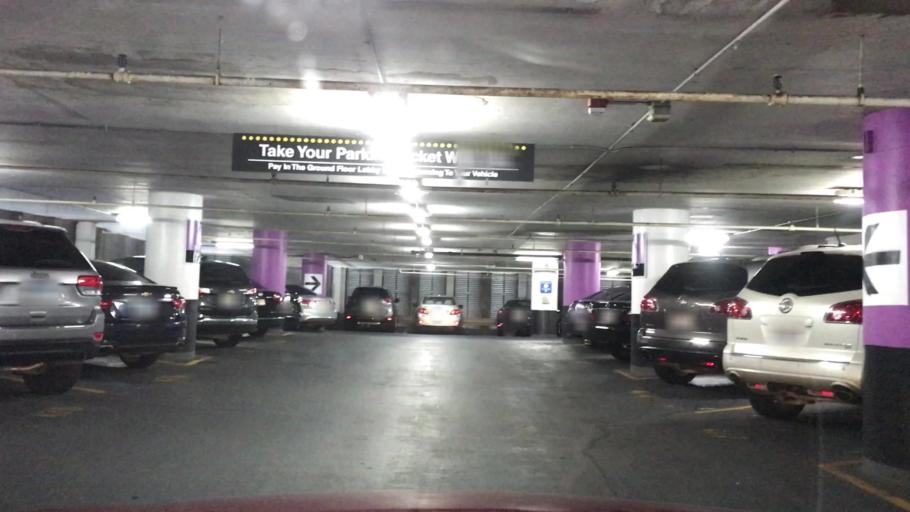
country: US
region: Illinois
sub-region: Cook County
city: Chicago
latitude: 41.8797
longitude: -87.6252
